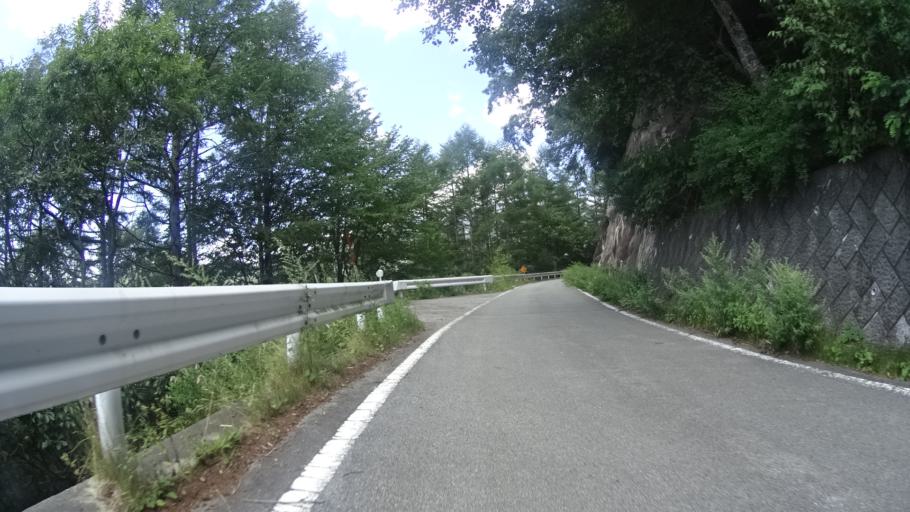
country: JP
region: Yamanashi
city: Enzan
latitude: 35.8309
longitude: 138.6390
